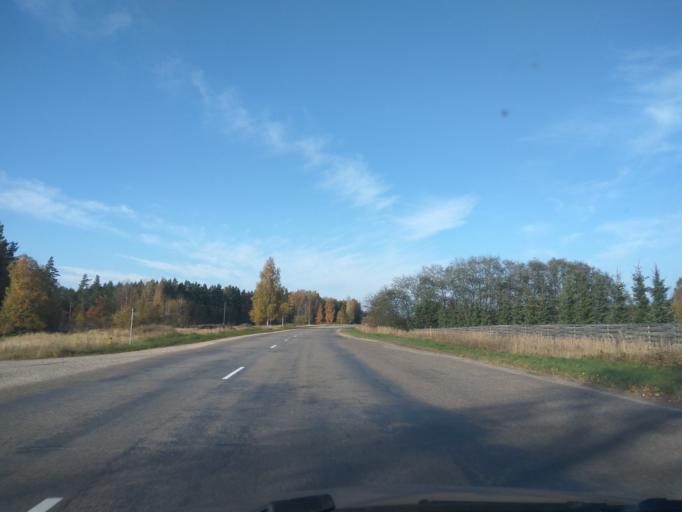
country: LV
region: Ventspils
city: Ventspils
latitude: 57.2848
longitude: 21.5700
